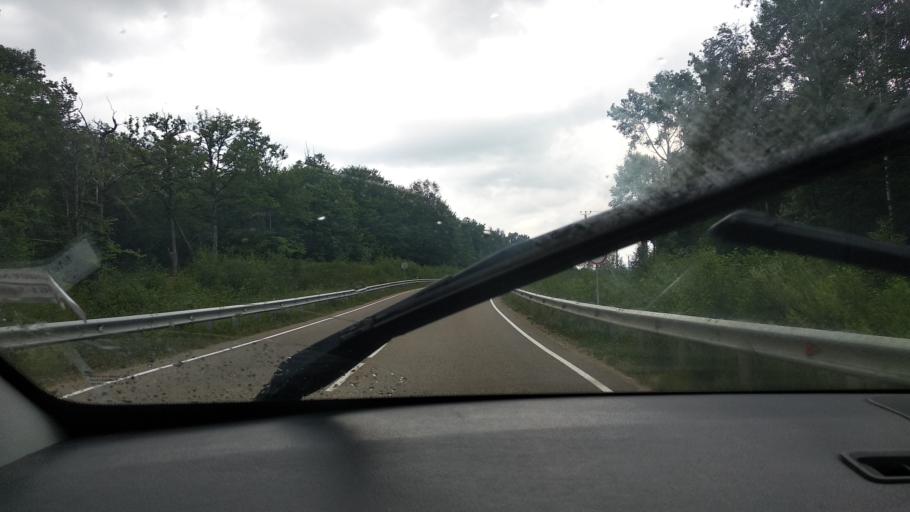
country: RU
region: Adygeya
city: Kamennomostskiy
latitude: 44.2691
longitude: 39.9408
